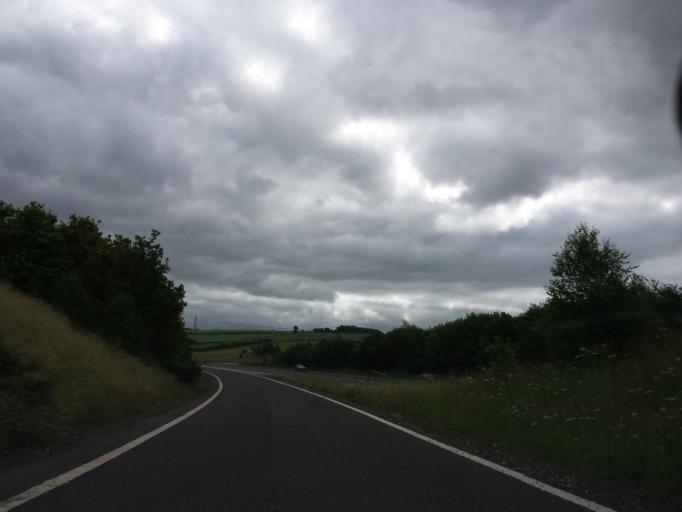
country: GB
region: Scotland
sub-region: East Lothian
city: Musselburgh
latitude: 55.9294
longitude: -3.0192
